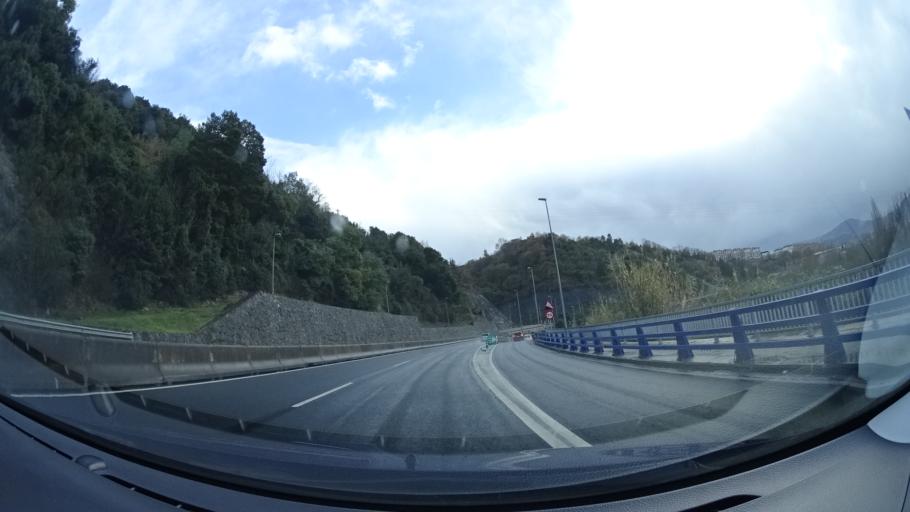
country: ES
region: Basque Country
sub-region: Bizkaia
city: Basauri
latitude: 43.2544
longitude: -2.8928
